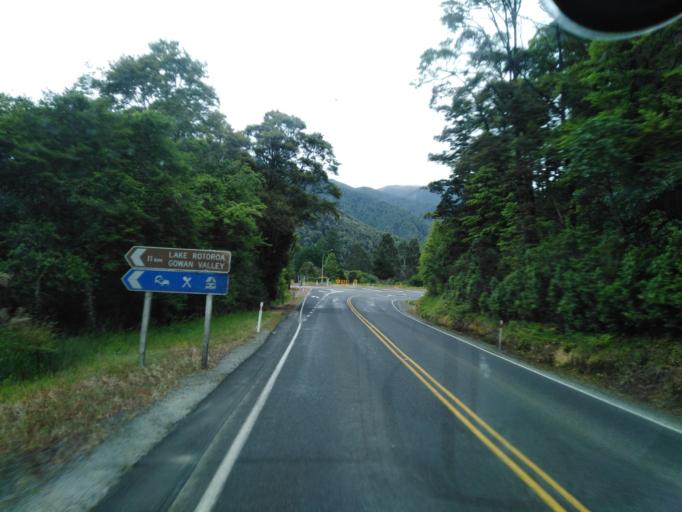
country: NZ
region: Tasman
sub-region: Tasman District
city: Wakefield
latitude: -41.7119
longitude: 172.5585
